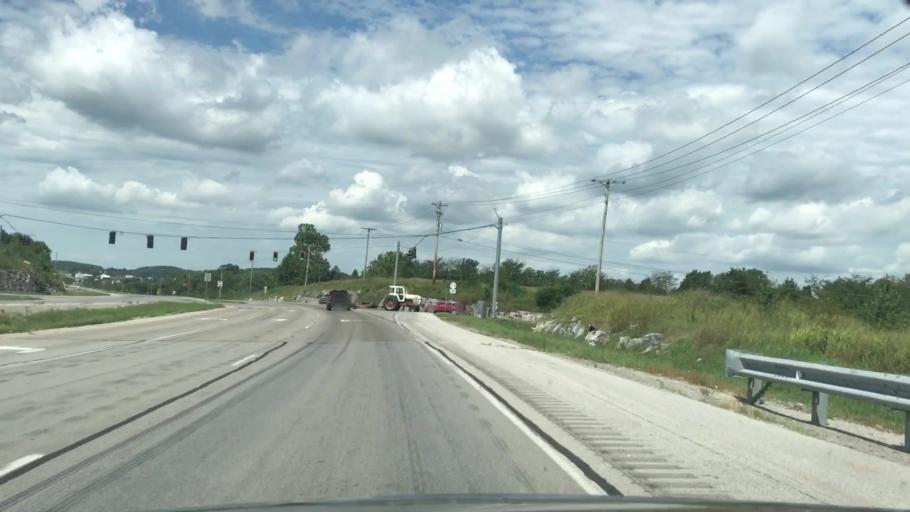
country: US
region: Kentucky
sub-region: Logan County
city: Russellville
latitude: 36.8651
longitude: -86.8672
